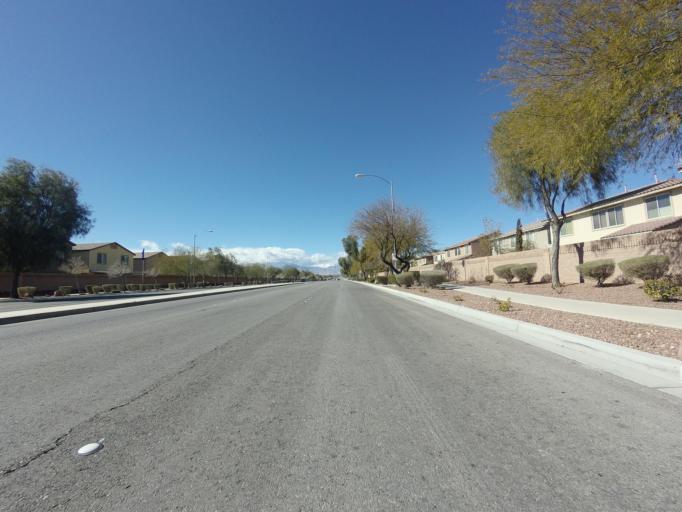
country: US
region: Nevada
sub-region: Clark County
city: Nellis Air Force Base
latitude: 36.2693
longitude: -115.0853
